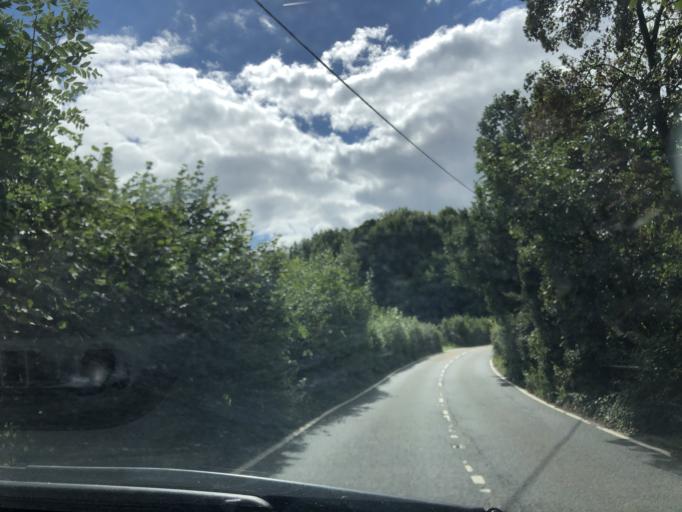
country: GB
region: England
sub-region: Kent
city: Westerham
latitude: 51.2501
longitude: 0.0783
